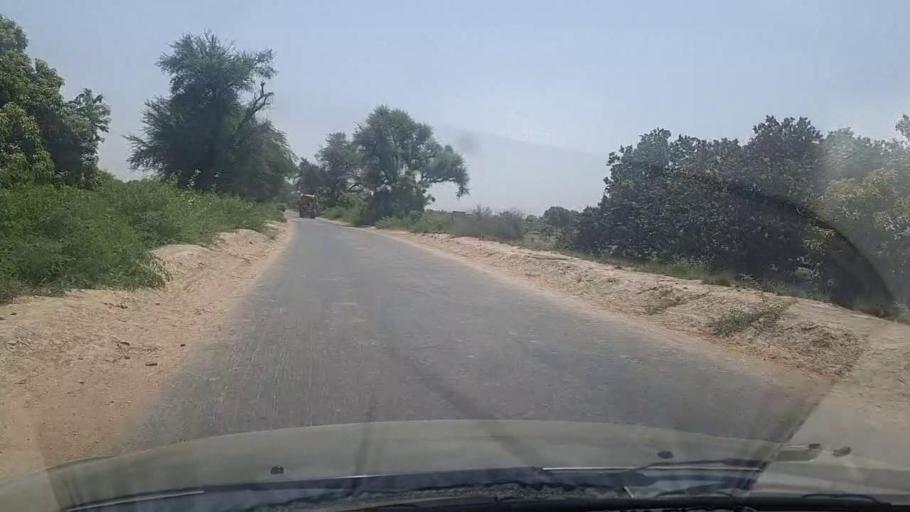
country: PK
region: Sindh
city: Tando Jam
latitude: 25.2838
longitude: 68.6005
